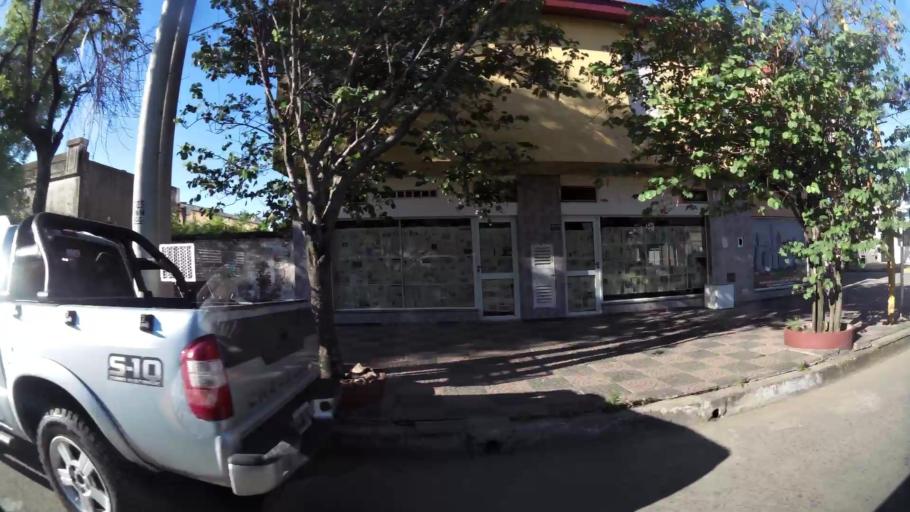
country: AR
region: Cordoba
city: San Francisco
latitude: -31.4349
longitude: -62.0898
